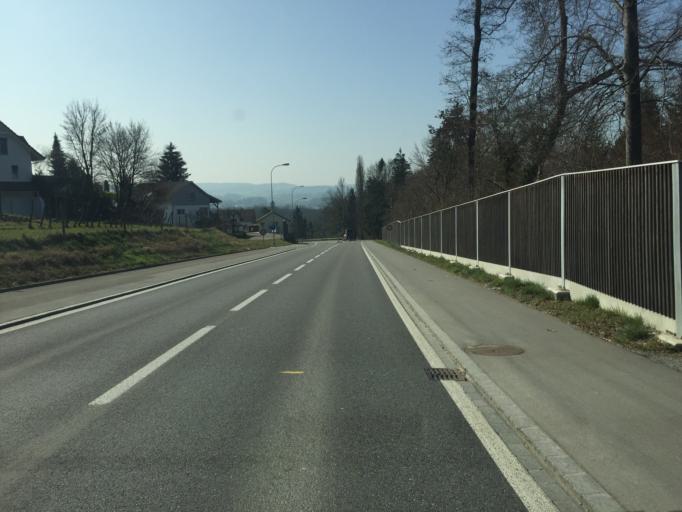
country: CH
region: Thurgau
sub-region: Frauenfeld District
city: Huttwilen
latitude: 47.5831
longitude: 8.8823
